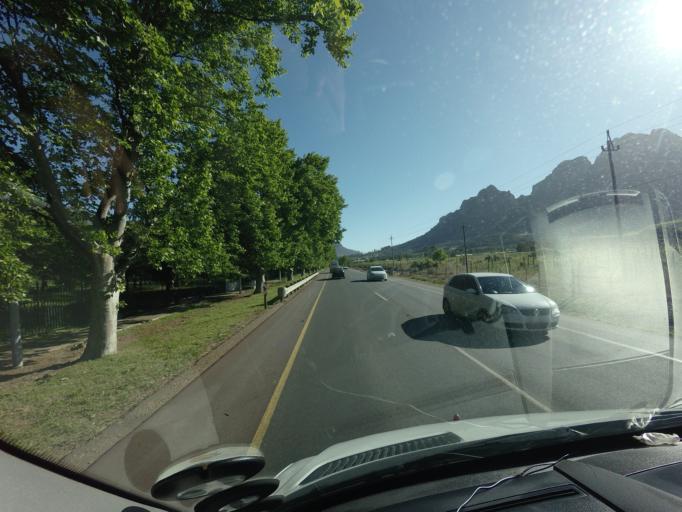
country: ZA
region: Western Cape
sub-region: Cape Winelands District Municipality
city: Stellenbosch
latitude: -33.8819
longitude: 18.9694
